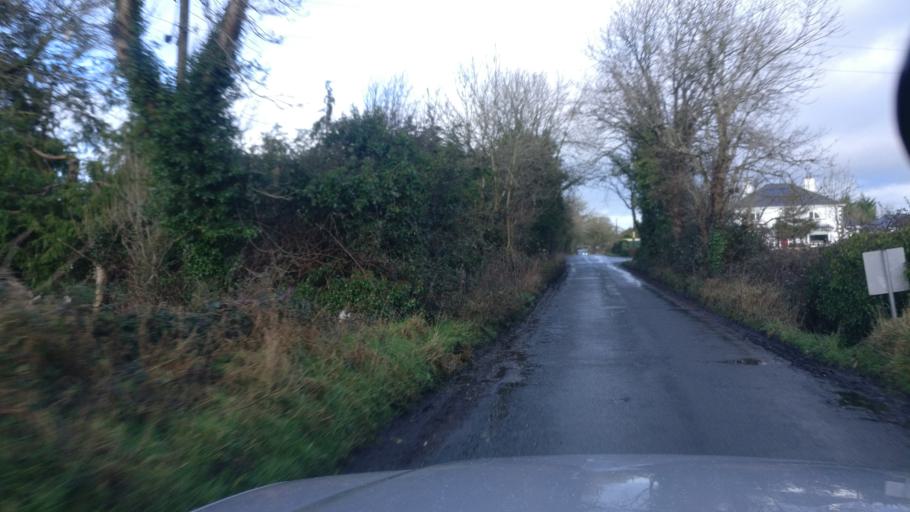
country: IE
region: Connaught
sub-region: County Galway
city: Loughrea
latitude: 53.2194
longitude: -8.5407
